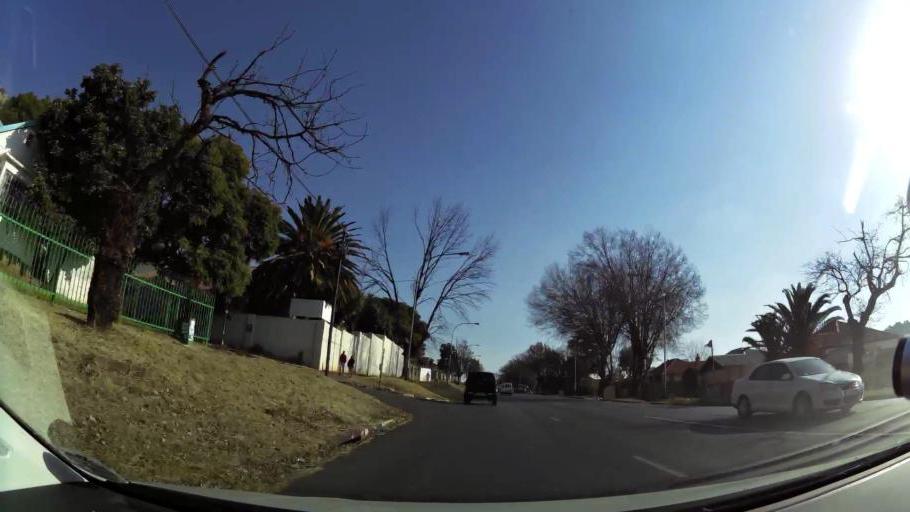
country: ZA
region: Gauteng
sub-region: City of Johannesburg Metropolitan Municipality
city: Johannesburg
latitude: -26.1922
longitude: 28.0829
